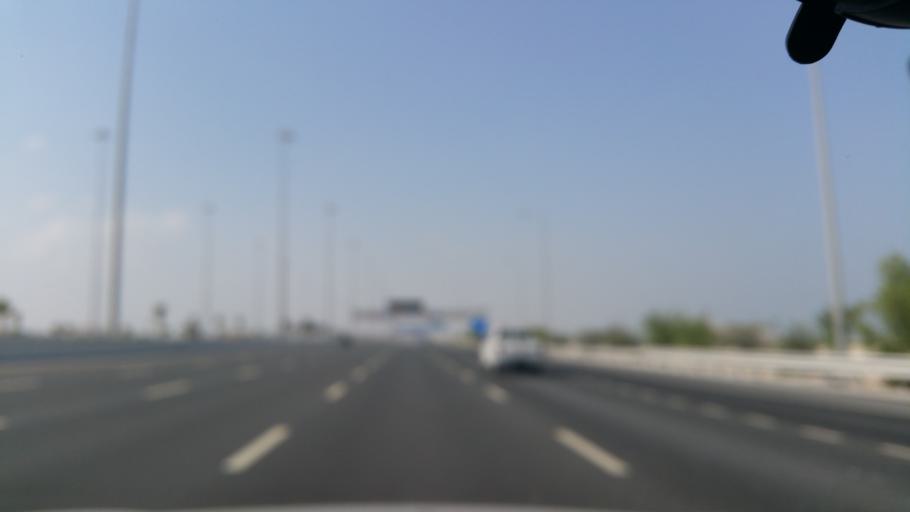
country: QA
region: Baladiyat Umm Salal
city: Umm Salal Muhammad
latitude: 25.4399
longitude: 51.4823
